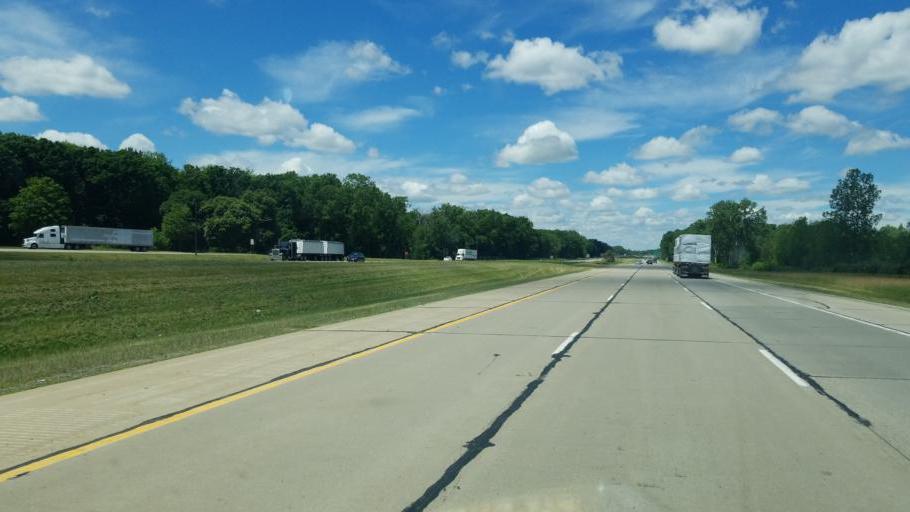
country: US
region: Michigan
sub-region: Livingston County
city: Howell
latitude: 42.6054
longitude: -83.9568
